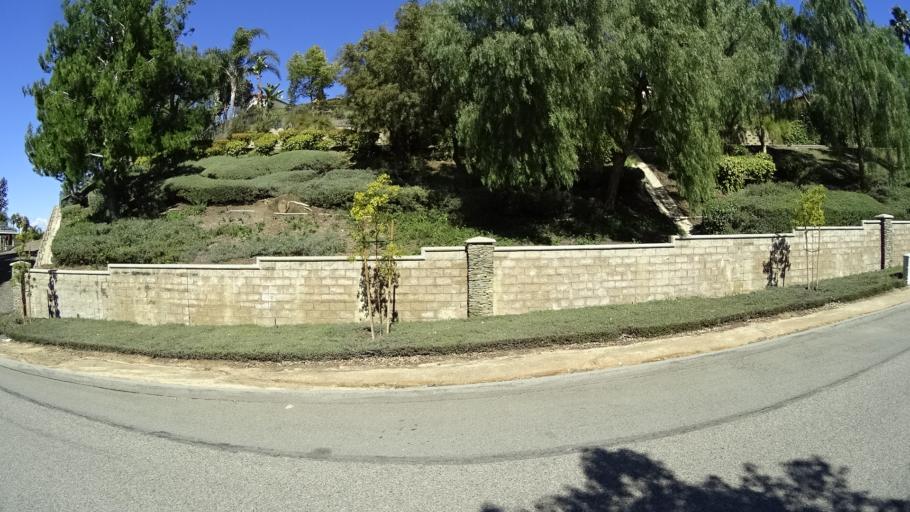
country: US
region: California
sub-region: Orange County
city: Villa Park
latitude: 33.8472
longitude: -117.8105
